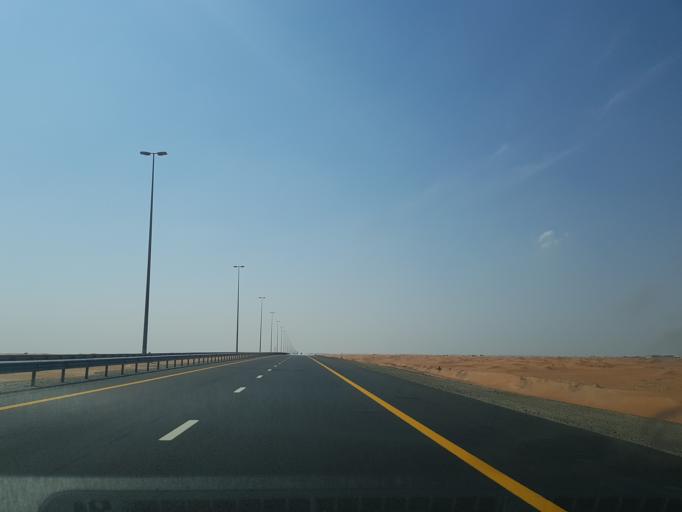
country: AE
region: Ash Shariqah
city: Adh Dhayd
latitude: 25.2533
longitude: 55.7622
